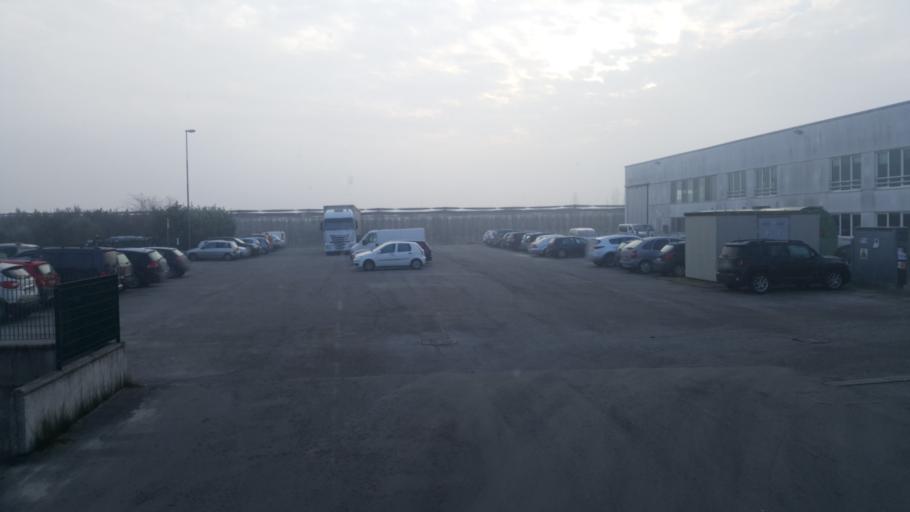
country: IT
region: Emilia-Romagna
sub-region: Provincia di Ravenna
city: Bagnacavallo
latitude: 44.4097
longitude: 12.0000
